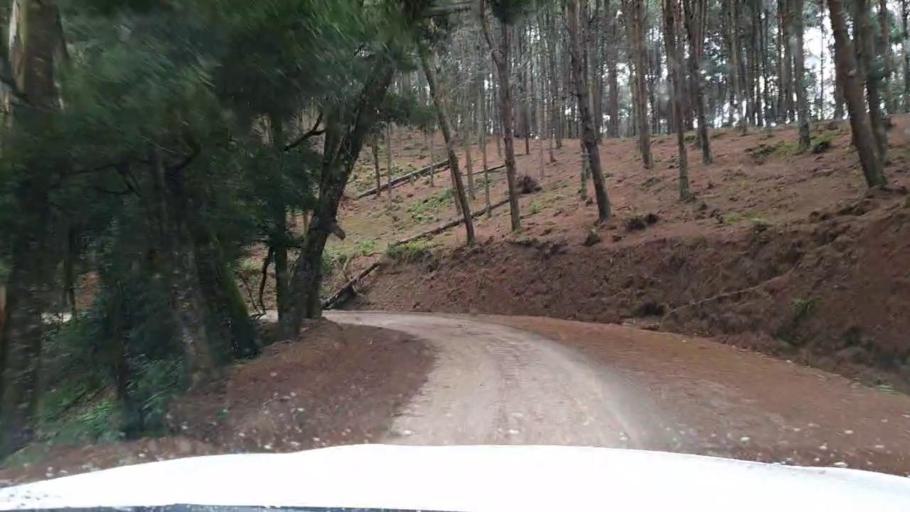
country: RW
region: Southern Province
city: Nzega
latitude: -2.3630
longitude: 29.3818
